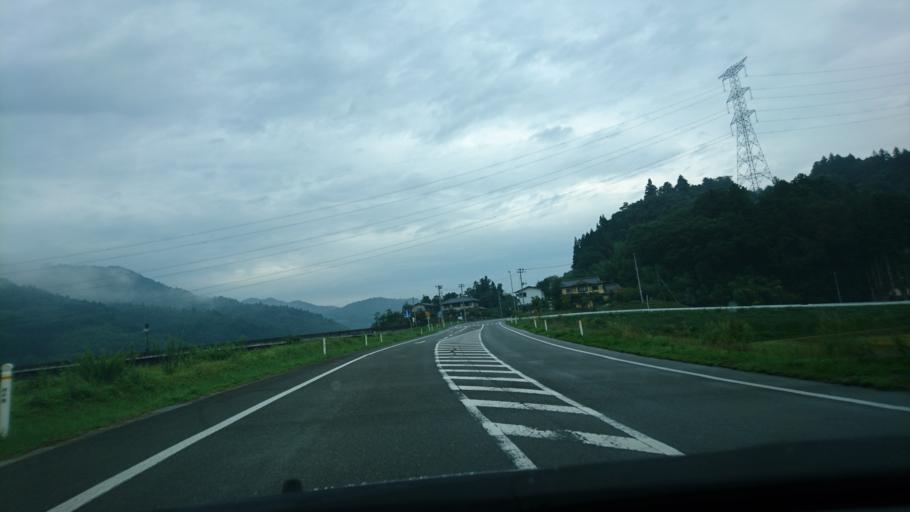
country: JP
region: Iwate
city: Ichinoseki
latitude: 38.9336
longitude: 141.2499
